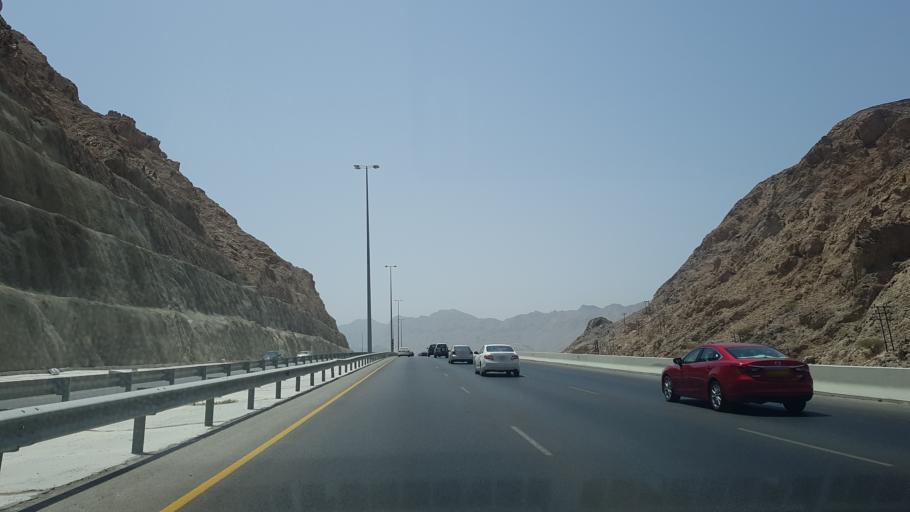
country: OM
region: Muhafazat Masqat
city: Muscat
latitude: 23.5393
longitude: 58.5203
